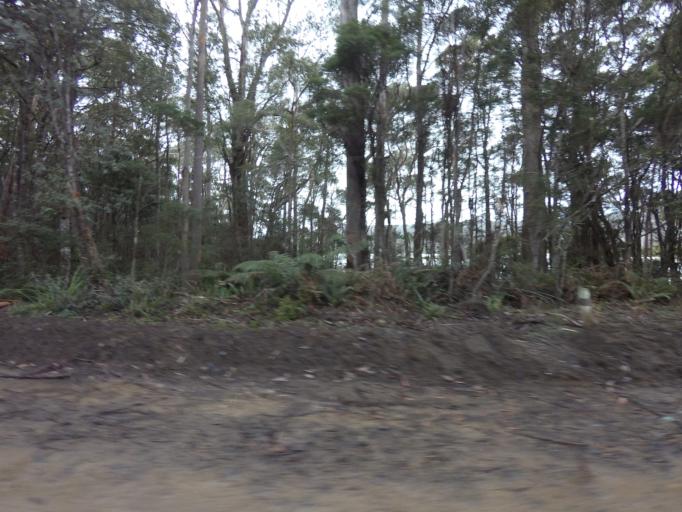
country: AU
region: Tasmania
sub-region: Huon Valley
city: Geeveston
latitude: -43.5768
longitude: 146.8875
